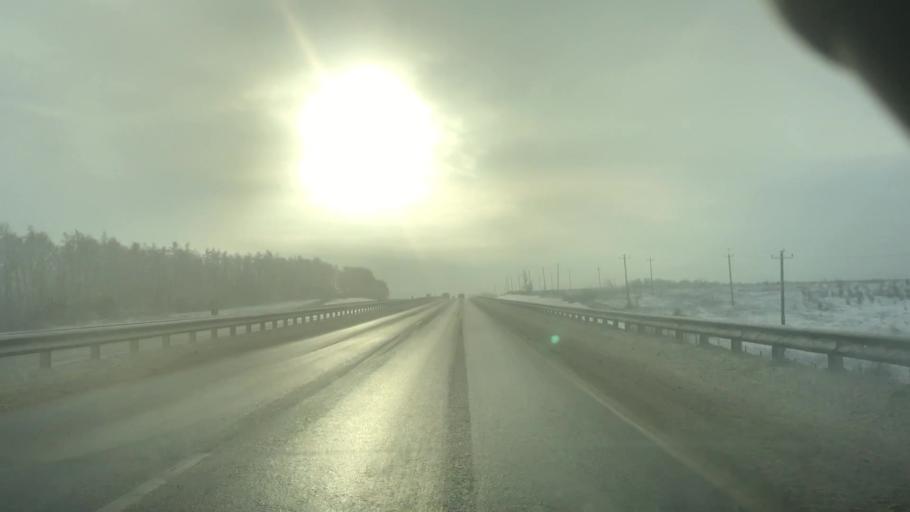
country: RU
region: Tula
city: Venev
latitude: 54.3184
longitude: 38.1544
